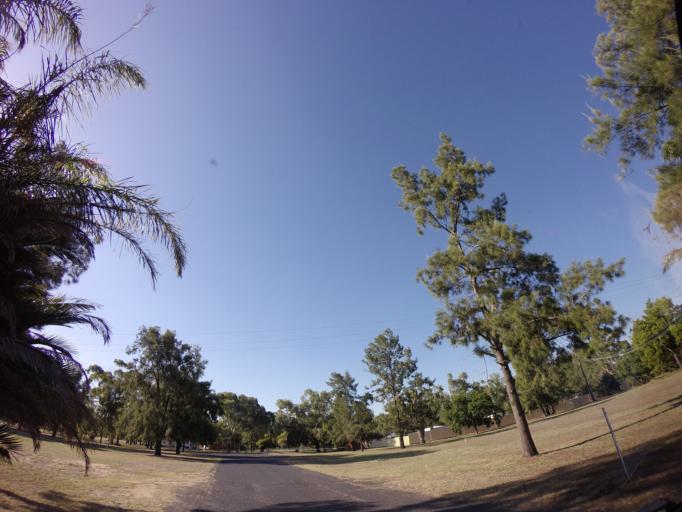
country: AU
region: New South Wales
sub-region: Gilgandra
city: Gilgandra
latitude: -31.7151
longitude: 148.6712
